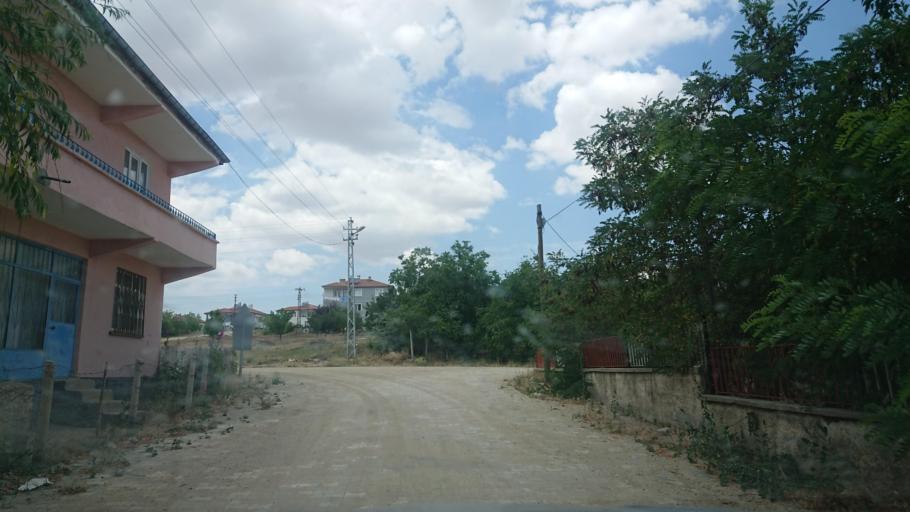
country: TR
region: Aksaray
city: Agacoren
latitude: 38.8725
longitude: 33.9078
